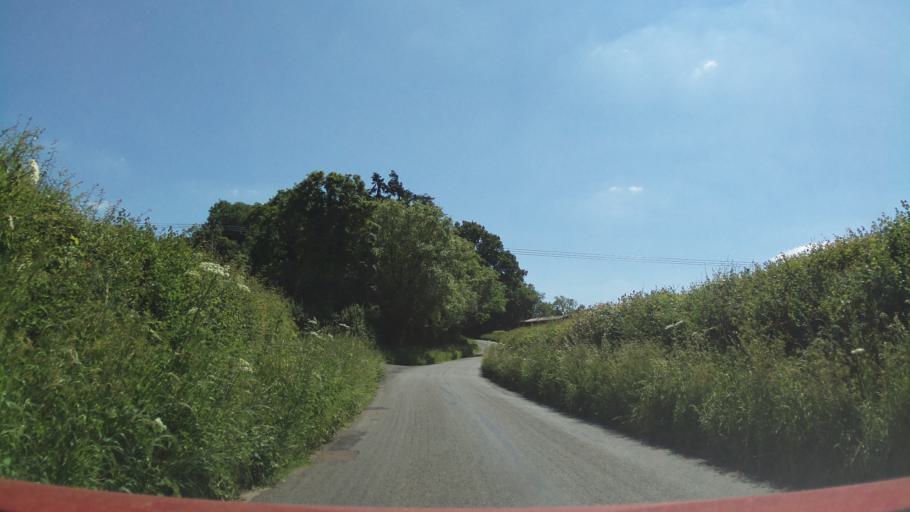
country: GB
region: England
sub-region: Wiltshire
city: Bremhill
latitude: 51.4432
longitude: -2.0240
